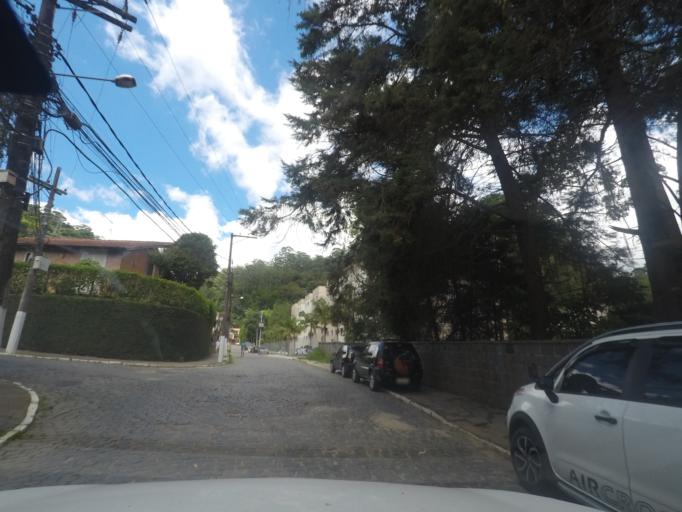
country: BR
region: Rio de Janeiro
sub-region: Teresopolis
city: Teresopolis
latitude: -22.4111
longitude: -42.9865
